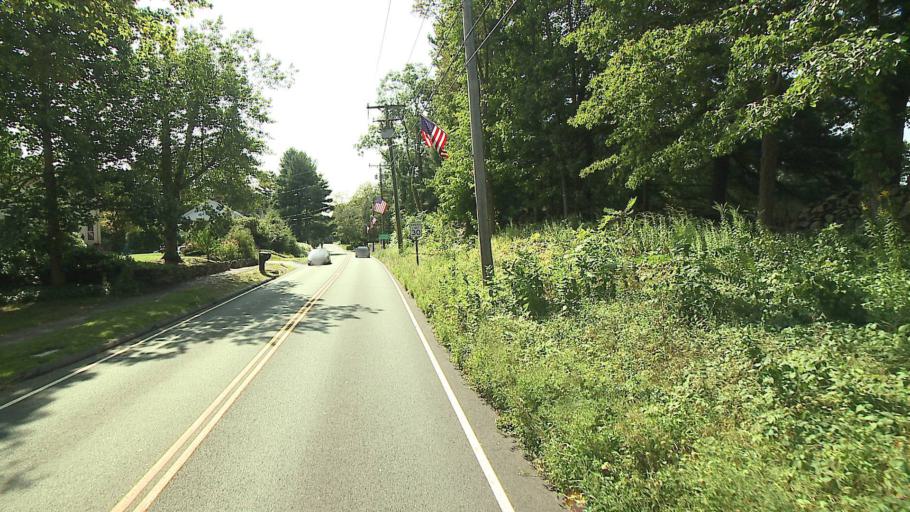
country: US
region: Connecticut
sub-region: Fairfield County
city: Danbury
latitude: 41.4649
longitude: -73.3869
